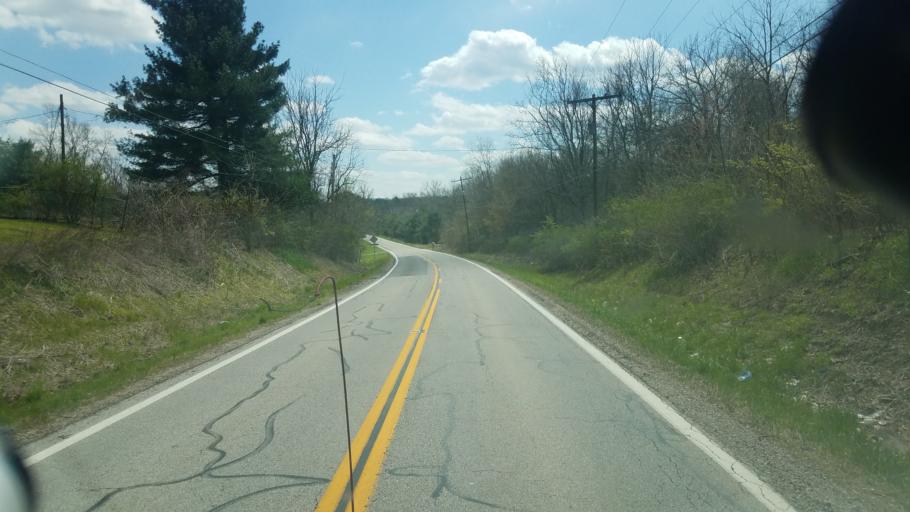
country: US
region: Ohio
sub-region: Licking County
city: Johnstown
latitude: 40.1207
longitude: -82.6599
